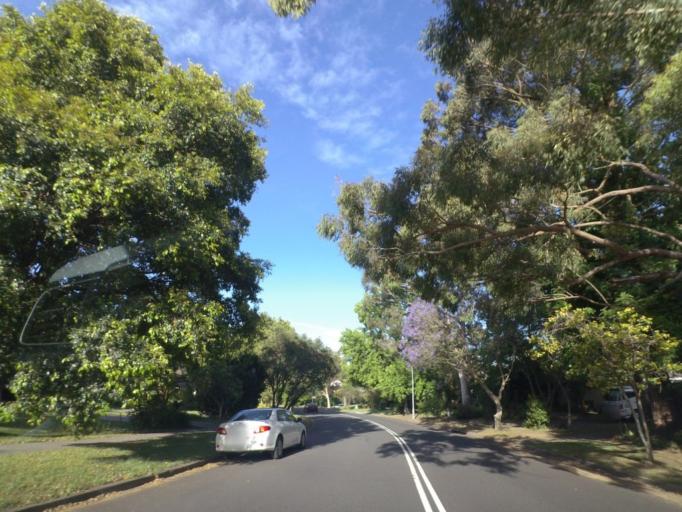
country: AU
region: New South Wales
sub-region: The Hills Shire
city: West Pennant
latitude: -33.7388
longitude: 151.0376
